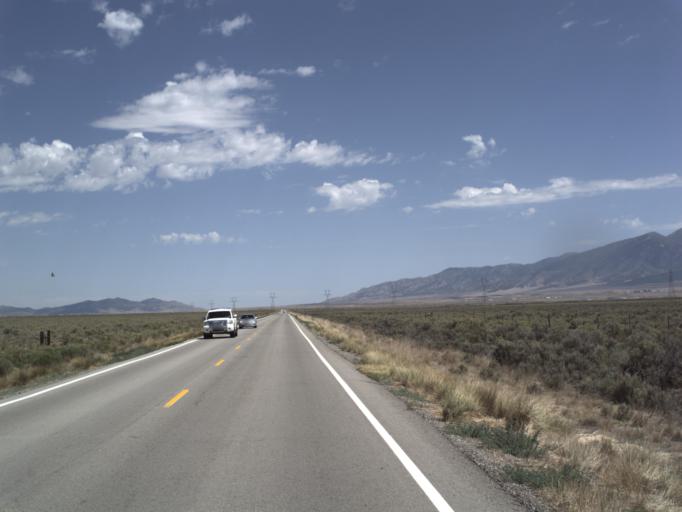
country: US
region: Utah
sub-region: Tooele County
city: Tooele
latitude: 40.2355
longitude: -112.4024
